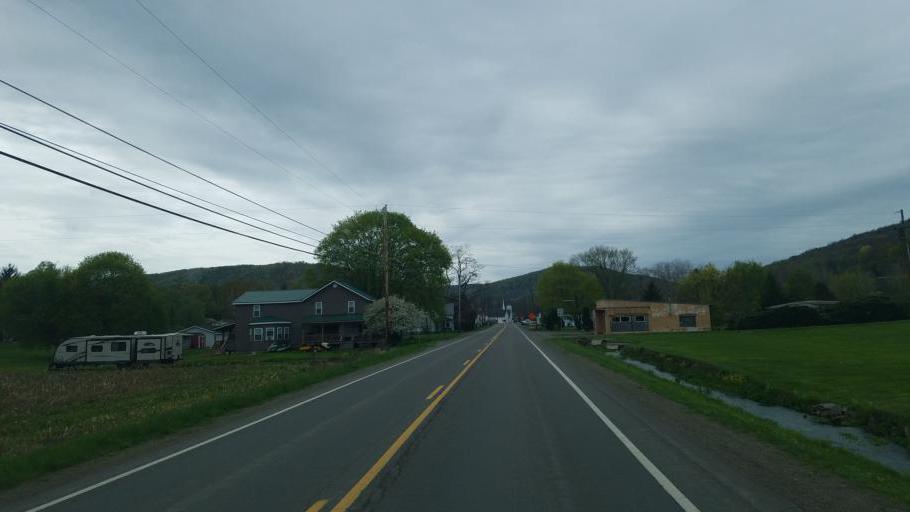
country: US
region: Pennsylvania
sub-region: Tioga County
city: Westfield
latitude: 41.9132
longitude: -77.5998
